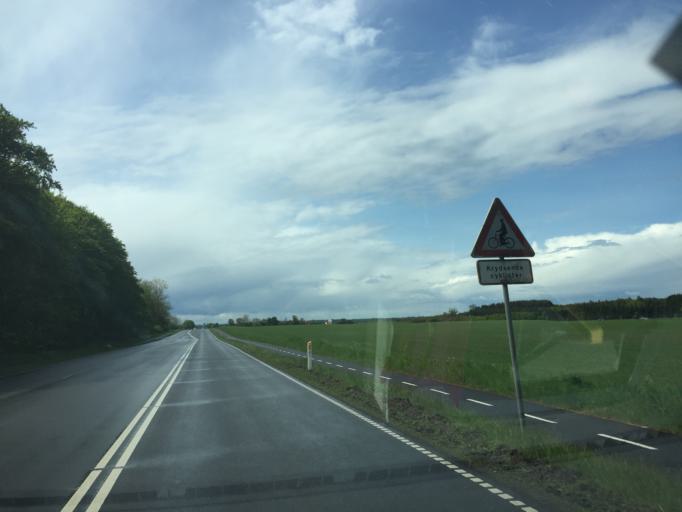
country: DK
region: Zealand
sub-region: Soro Kommune
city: Soro
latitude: 55.4337
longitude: 11.4879
